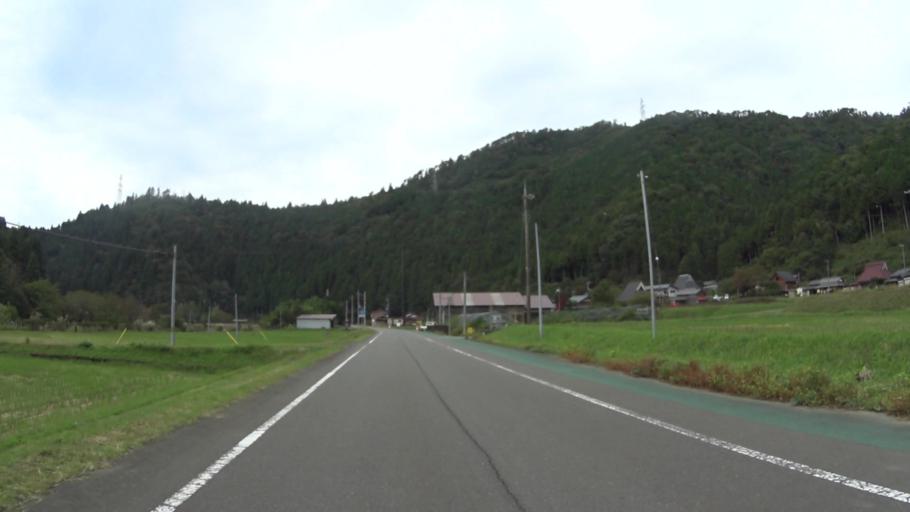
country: JP
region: Fukui
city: Obama
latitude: 35.3199
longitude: 135.6564
